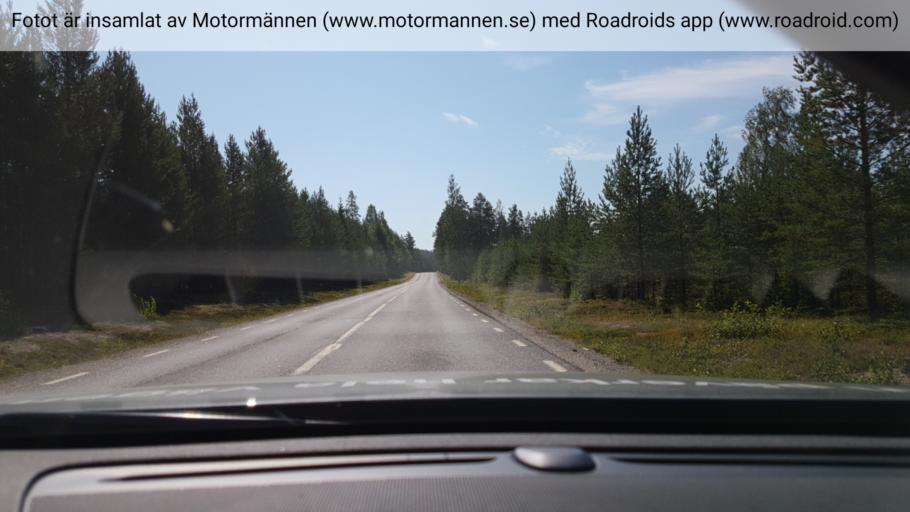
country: SE
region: Vaesterbotten
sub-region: Vindelns Kommun
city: Vindeln
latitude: 64.2731
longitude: 19.6339
